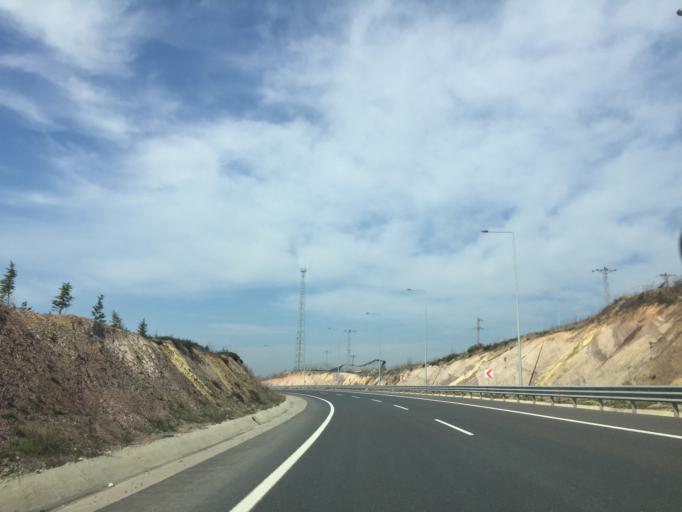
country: TR
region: Istanbul
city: Sancaktepe
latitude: 41.0474
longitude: 29.2781
